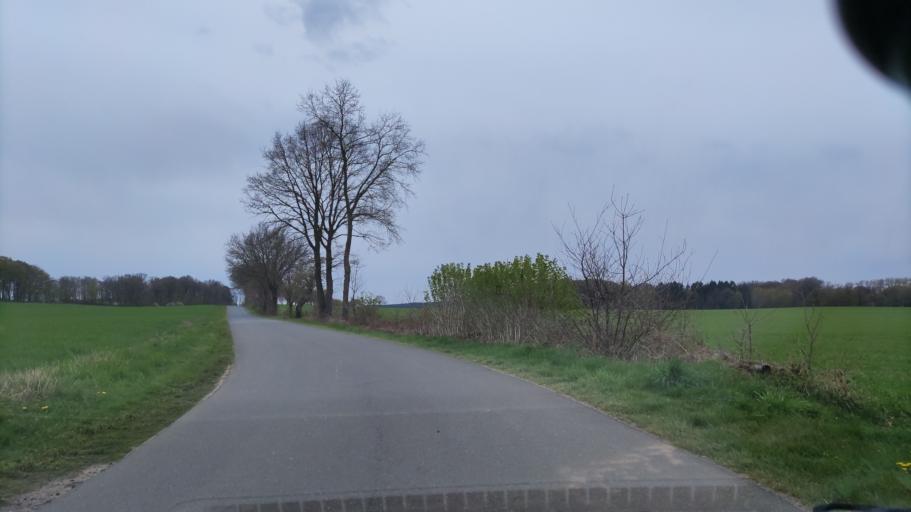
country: DE
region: Lower Saxony
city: Oldendorf
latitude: 53.1696
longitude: 10.2395
